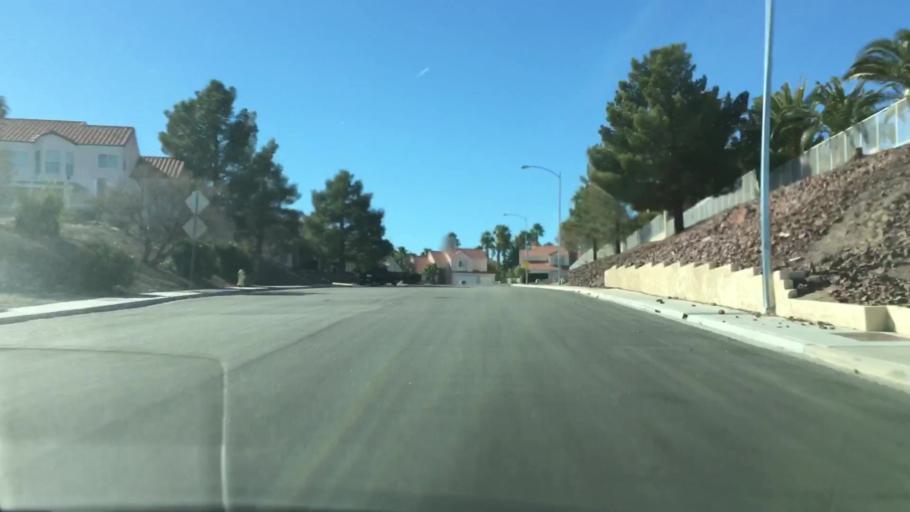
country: US
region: Nevada
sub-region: Clark County
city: Whitney
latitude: 36.0606
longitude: -115.0621
